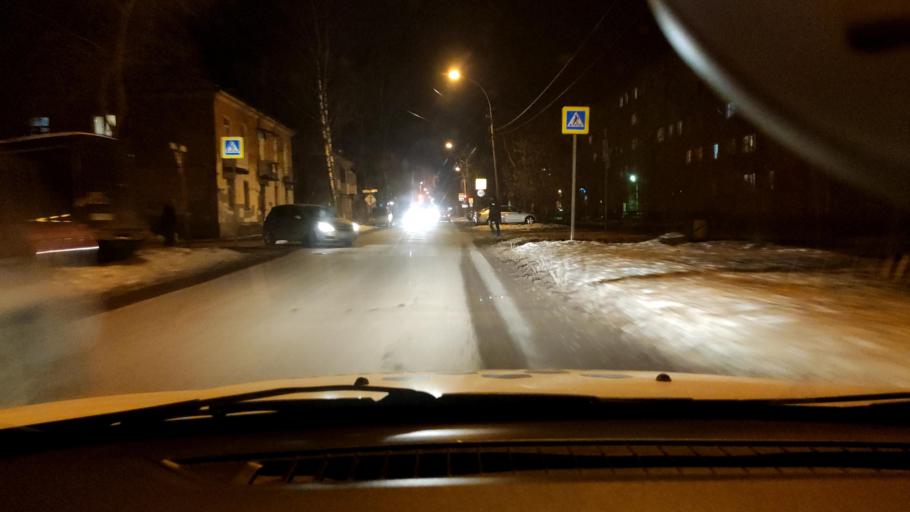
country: RU
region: Perm
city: Overyata
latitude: 58.0077
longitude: 55.9360
